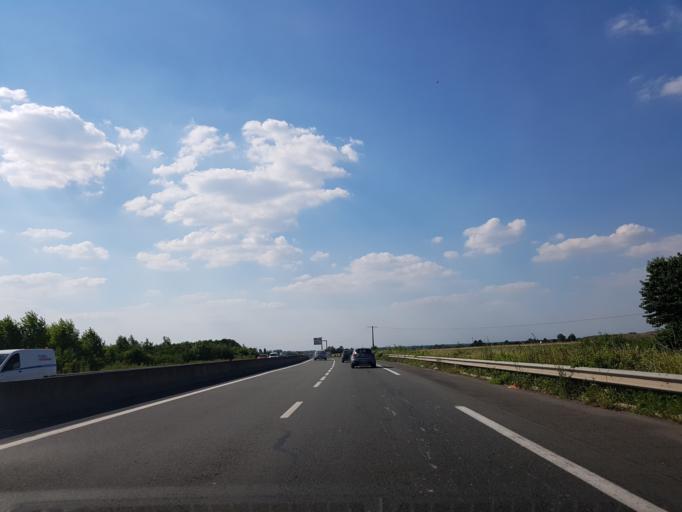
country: FR
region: Nord-Pas-de-Calais
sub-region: Departement du Nord
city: Abscon
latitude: 50.3390
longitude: 3.3185
